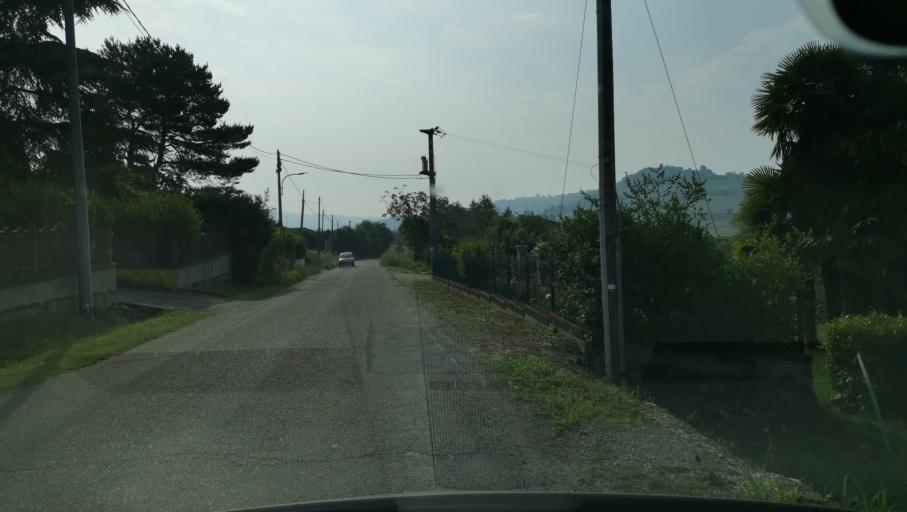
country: IT
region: Piedmont
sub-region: Provincia di Alessandria
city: Castelletto Merli
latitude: 45.0658
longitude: 8.2349
